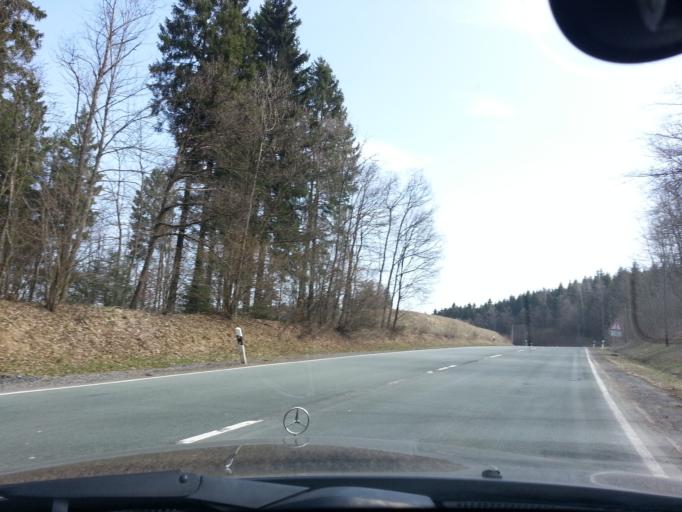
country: DE
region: North Rhine-Westphalia
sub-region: Regierungsbezirk Arnsberg
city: Bad Fredeburg
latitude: 51.2156
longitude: 8.3457
